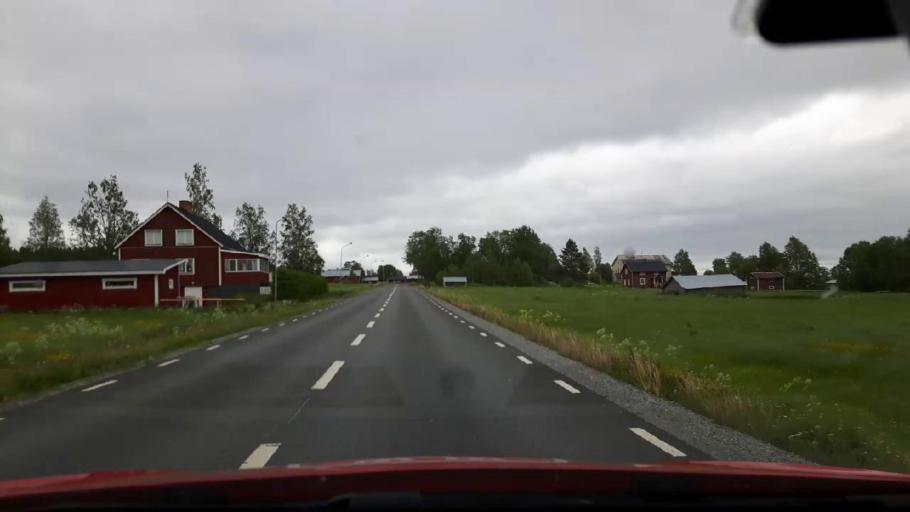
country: SE
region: Jaemtland
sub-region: OEstersunds Kommun
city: Lit
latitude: 63.7408
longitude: 14.8566
